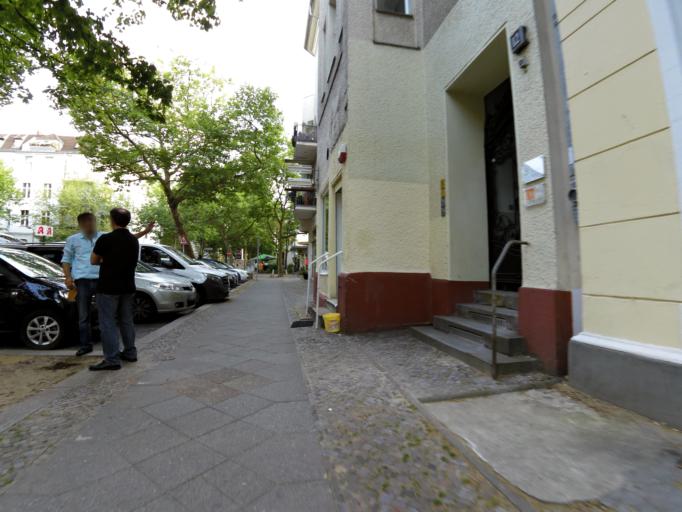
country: DE
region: Berlin
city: Schoneberg Bezirk
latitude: 52.4674
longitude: 13.3422
